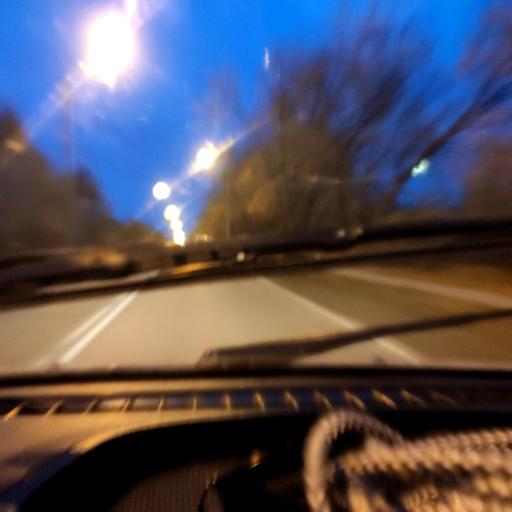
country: RU
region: Samara
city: Zhigulevsk
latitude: 53.4636
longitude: 49.5589
